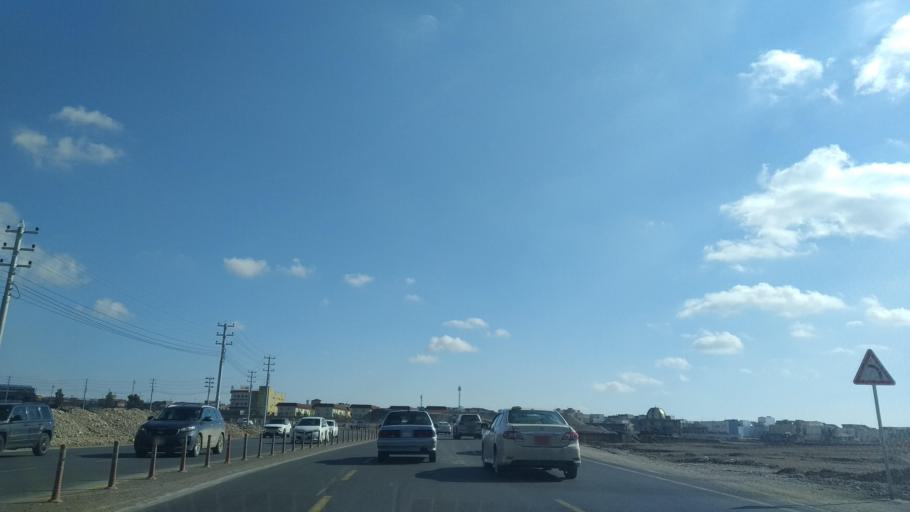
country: IQ
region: Arbil
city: Erbil
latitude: 36.2060
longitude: 44.1276
